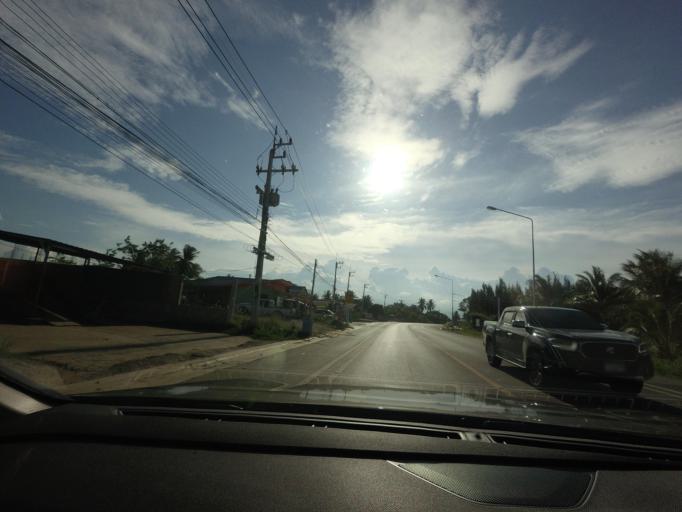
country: TH
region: Prachuap Khiri Khan
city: Pran Buri
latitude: 12.4073
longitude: 99.9627
